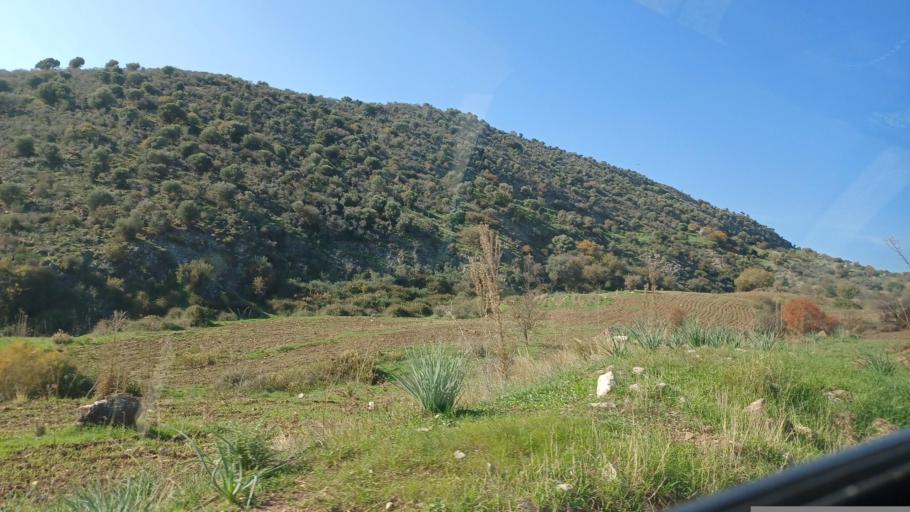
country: CY
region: Pafos
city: Mesogi
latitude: 34.7725
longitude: 32.5550
